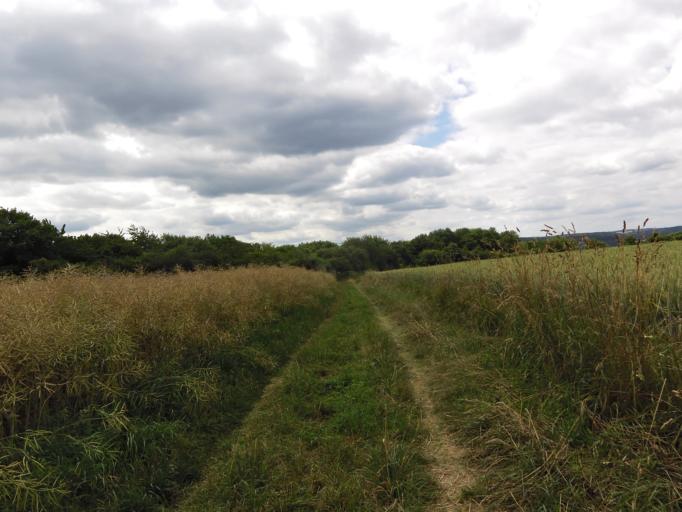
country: DE
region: Bavaria
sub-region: Regierungsbezirk Unterfranken
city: Randersacker
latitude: 49.7690
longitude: 9.9691
